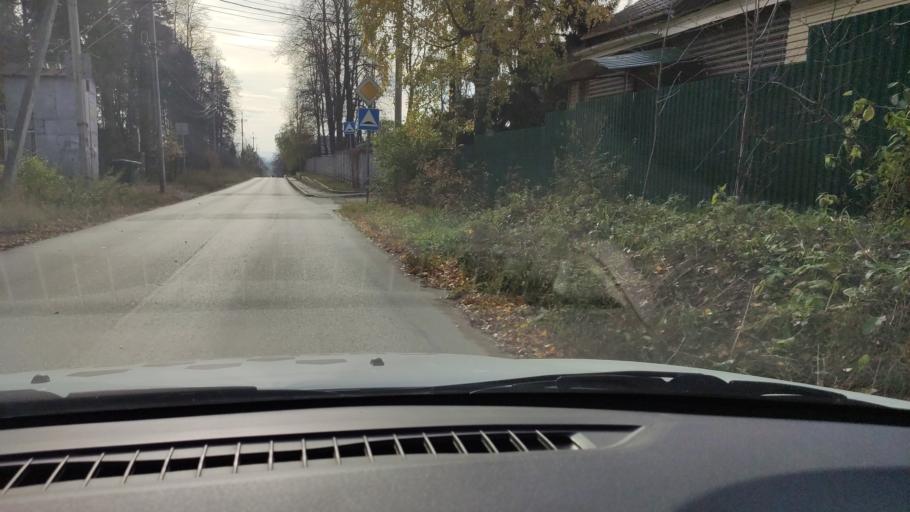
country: RU
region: Perm
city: Kondratovo
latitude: 58.0527
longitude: 56.1219
